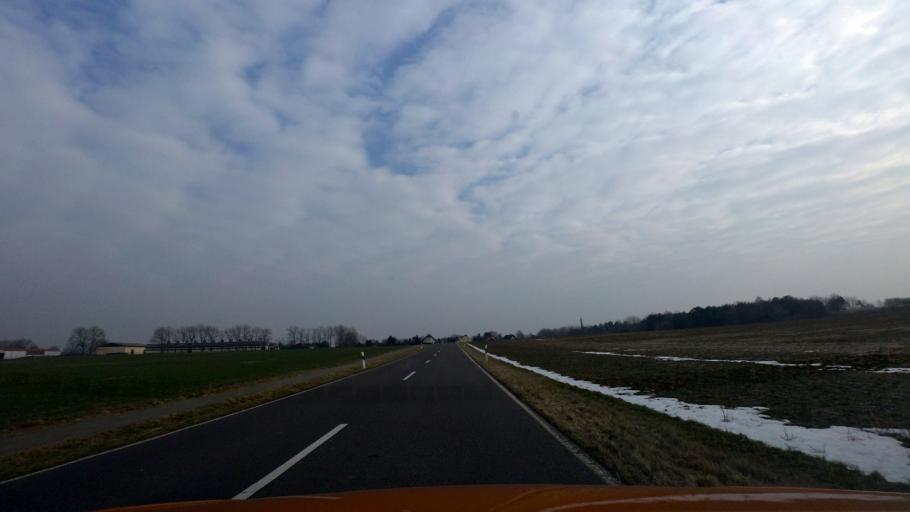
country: DE
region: Brandenburg
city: Rangsdorf
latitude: 52.2462
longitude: 13.3742
